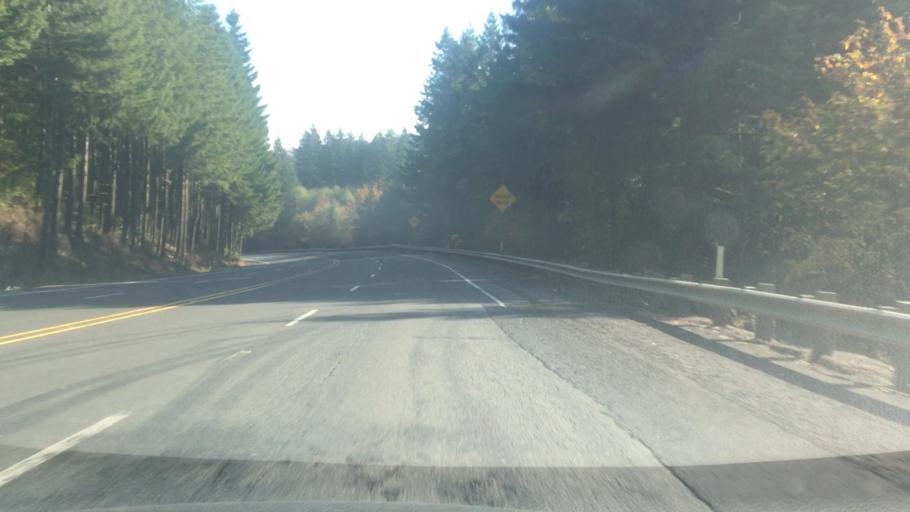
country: US
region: Oregon
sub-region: Polk County
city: Grand Ronde
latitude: 45.0592
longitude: -123.6870
